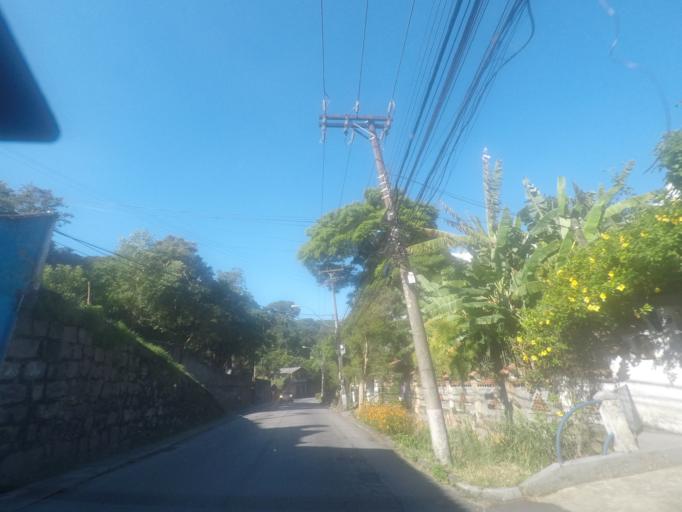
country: BR
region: Rio de Janeiro
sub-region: Petropolis
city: Petropolis
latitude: -22.5249
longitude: -43.1860
